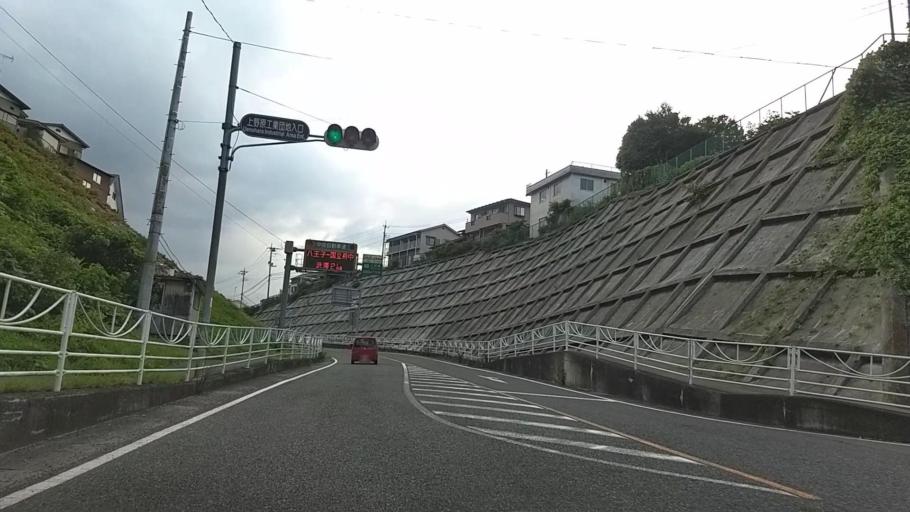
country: JP
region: Yamanashi
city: Uenohara
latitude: 35.6242
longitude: 139.1219
